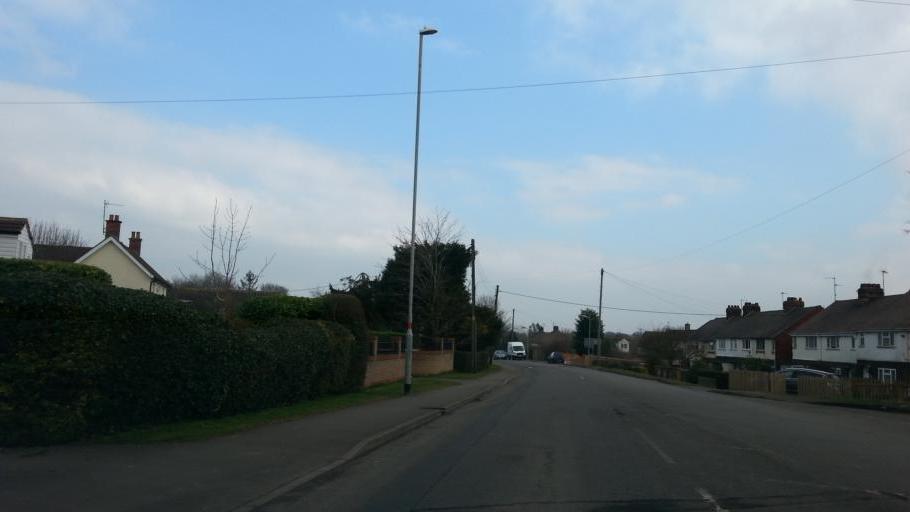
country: GB
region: England
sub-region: Northamptonshire
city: Corby
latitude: 52.4957
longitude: -0.6498
